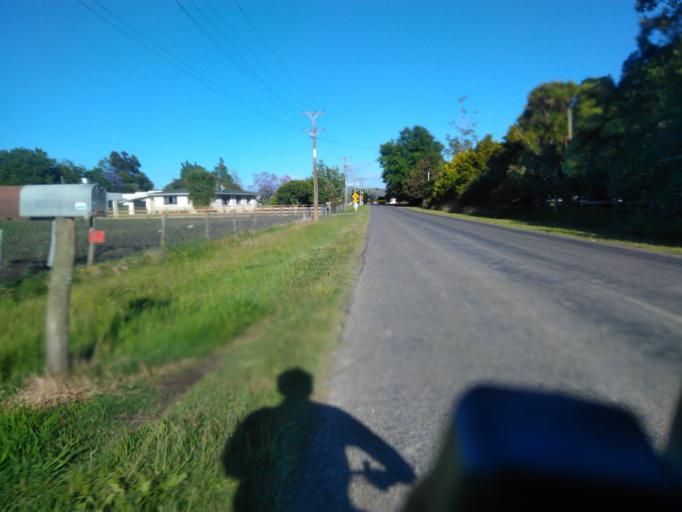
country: NZ
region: Gisborne
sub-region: Gisborne District
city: Gisborne
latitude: -38.5981
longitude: 177.9274
